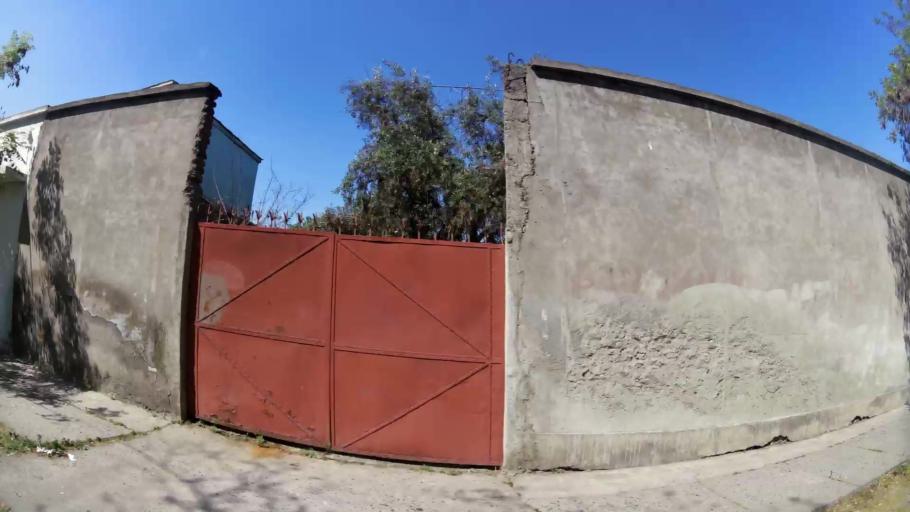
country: CL
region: Santiago Metropolitan
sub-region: Provincia de Santiago
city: Santiago
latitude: -33.5143
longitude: -70.6447
